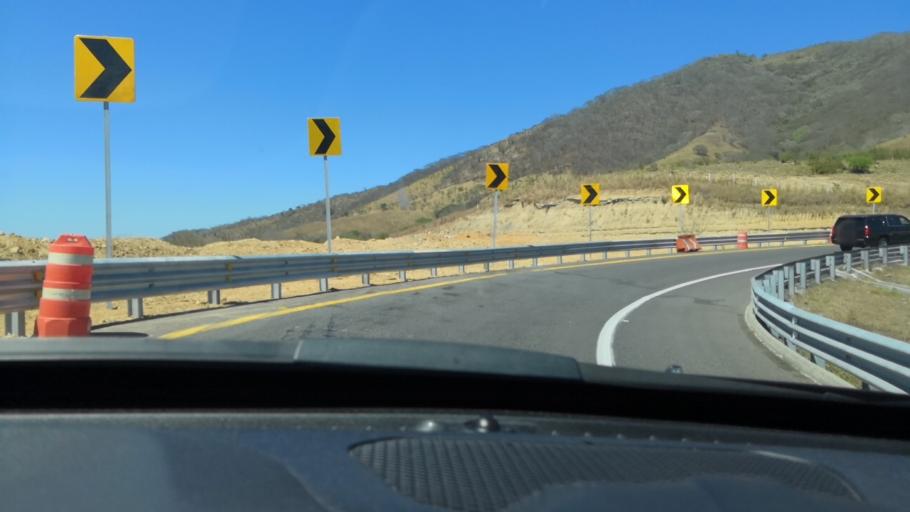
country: MX
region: Nayarit
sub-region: Compostela
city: Juan Escutia (Borbollon)
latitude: 21.1393
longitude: -104.9244
